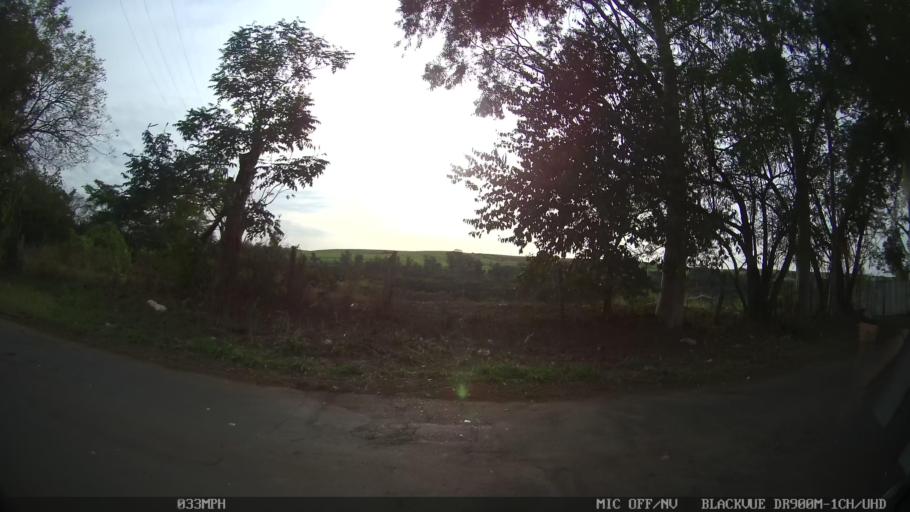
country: BR
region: Sao Paulo
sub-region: Piracicaba
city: Piracicaba
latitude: -22.6937
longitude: -47.5835
